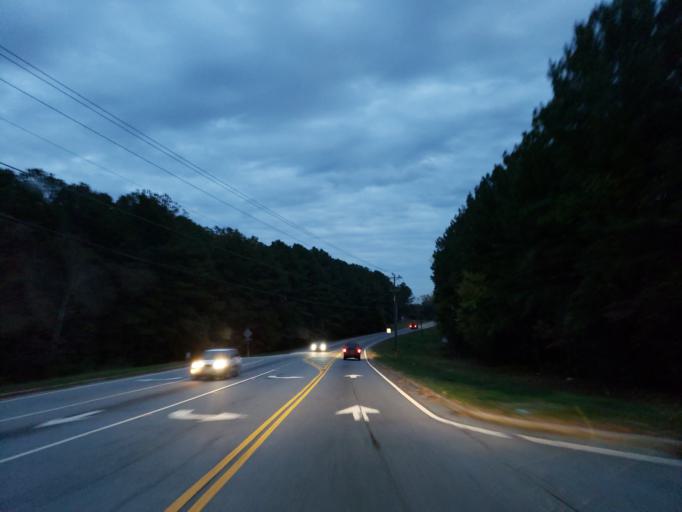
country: US
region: Georgia
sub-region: Cobb County
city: Powder Springs
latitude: 33.9397
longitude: -84.7024
